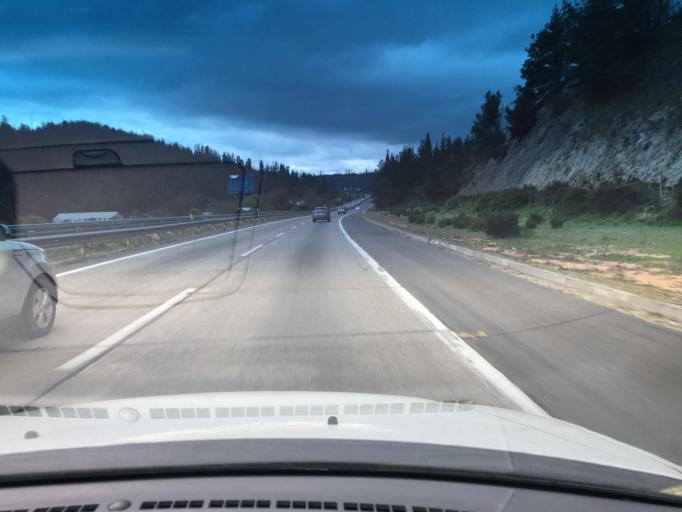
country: CL
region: Valparaiso
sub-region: Provincia de Marga Marga
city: Quilpue
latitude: -33.2280
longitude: -71.4672
